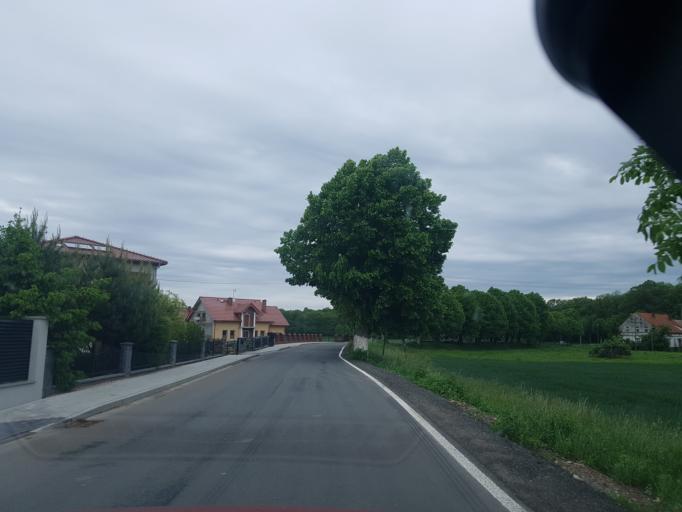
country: PL
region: Lower Silesian Voivodeship
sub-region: Powiat wroclawski
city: Katy Wroclawskie
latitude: 50.9805
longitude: 16.7525
